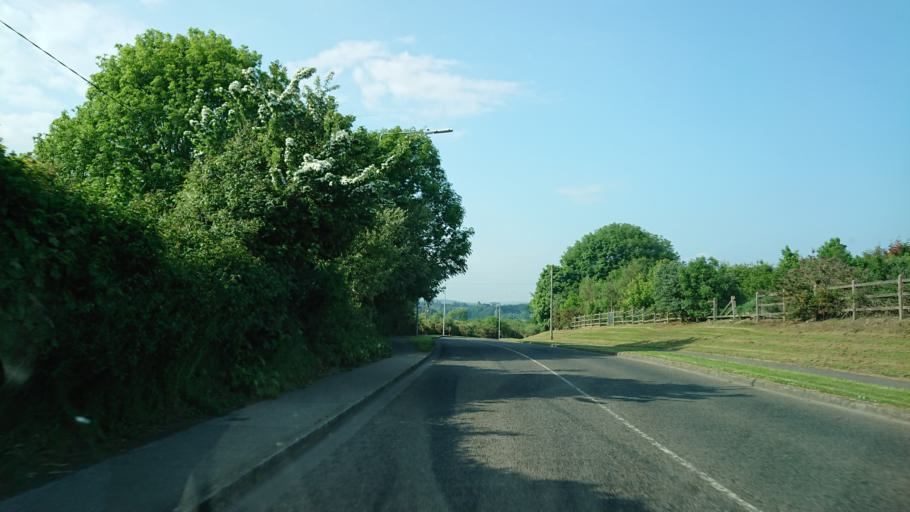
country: IE
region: Munster
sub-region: Waterford
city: Waterford
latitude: 52.2333
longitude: -7.0616
